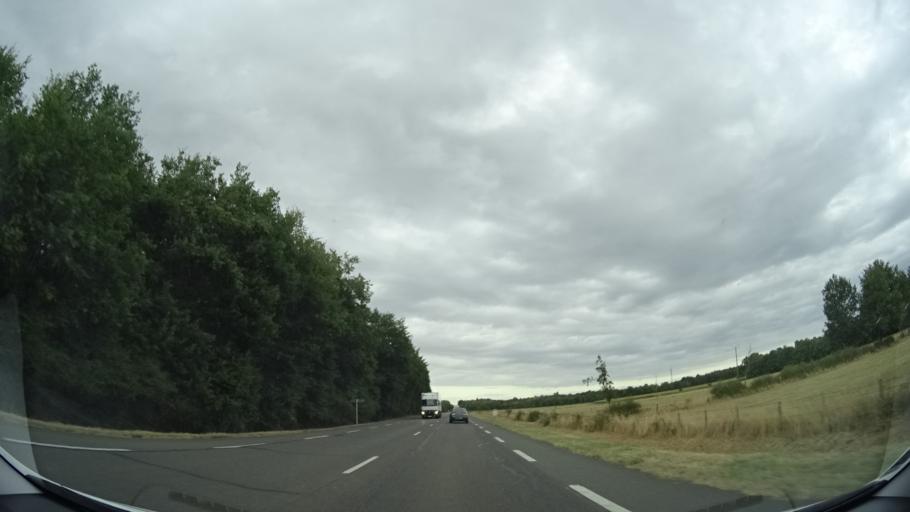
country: FR
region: Centre
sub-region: Departement du Loiret
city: Vitry-aux-Loges
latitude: 47.8958
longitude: 2.2765
